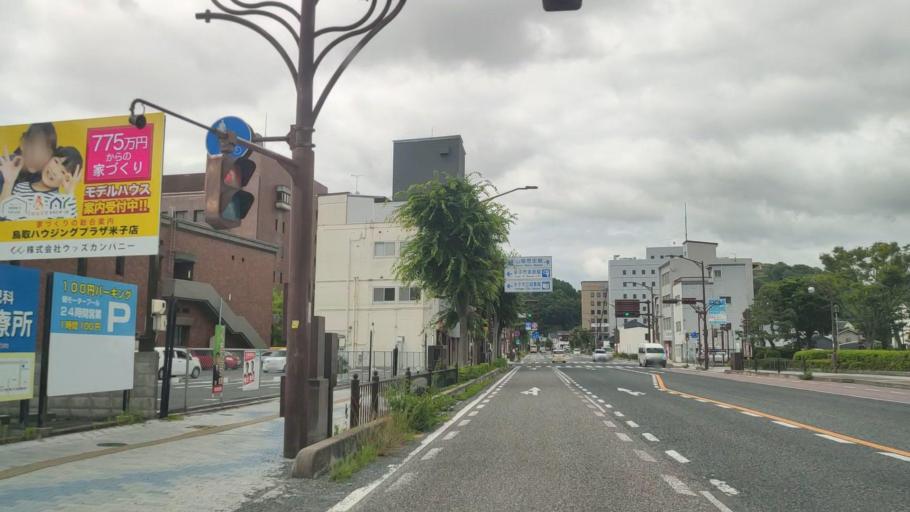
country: JP
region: Tottori
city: Yonago
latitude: 35.4293
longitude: 133.3309
